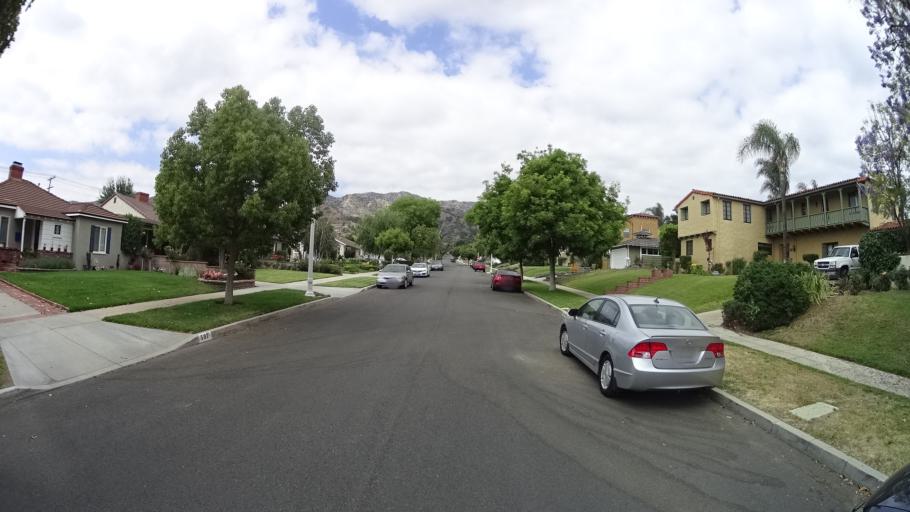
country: US
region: California
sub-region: Los Angeles County
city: Burbank
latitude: 34.1960
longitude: -118.3206
